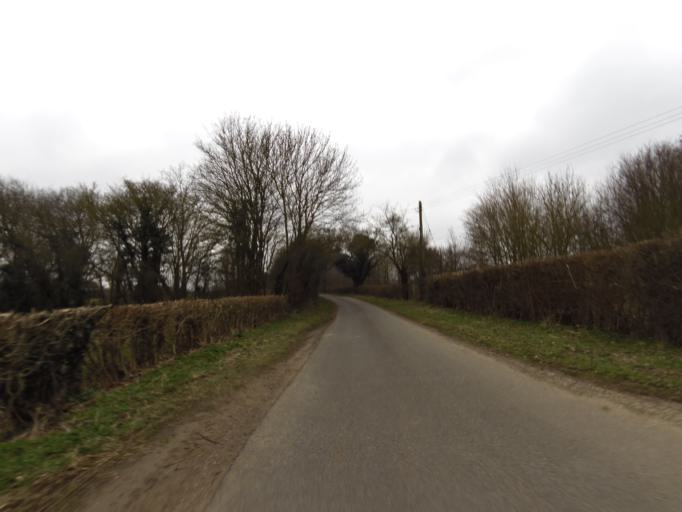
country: GB
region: England
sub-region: Suffolk
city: Framlingham
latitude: 52.1958
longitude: 1.3233
